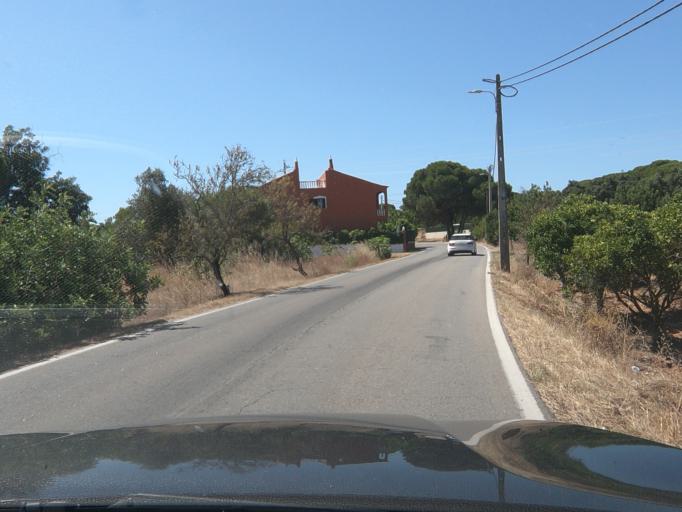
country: PT
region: Faro
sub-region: Loule
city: Vilamoura
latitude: 37.1010
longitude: -8.0969
